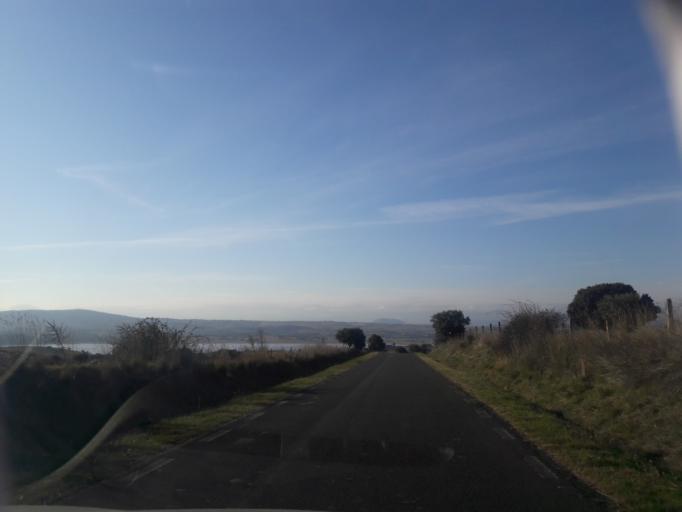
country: ES
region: Castille and Leon
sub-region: Provincia de Salamanca
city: Salvatierra de Tormes
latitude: 40.6007
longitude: -5.5997
